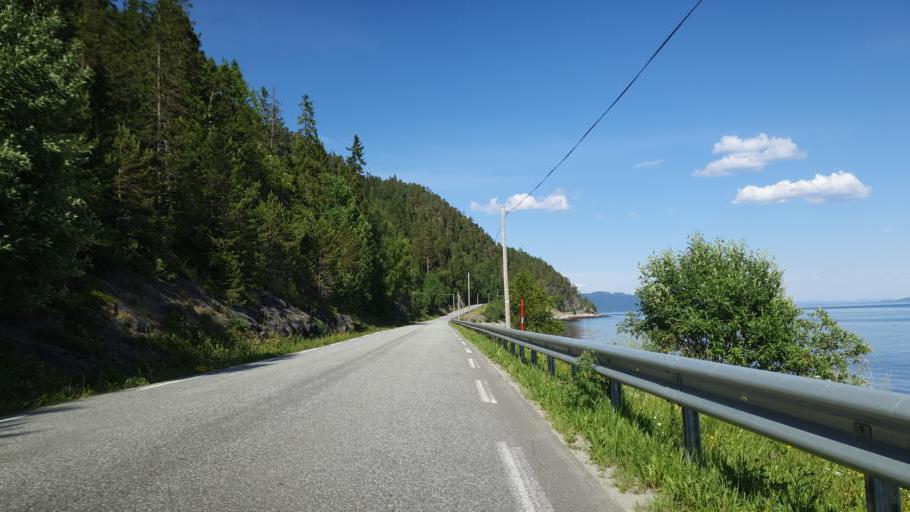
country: NO
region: Nord-Trondelag
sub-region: Leksvik
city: Leksvik
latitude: 63.6409
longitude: 10.5896
